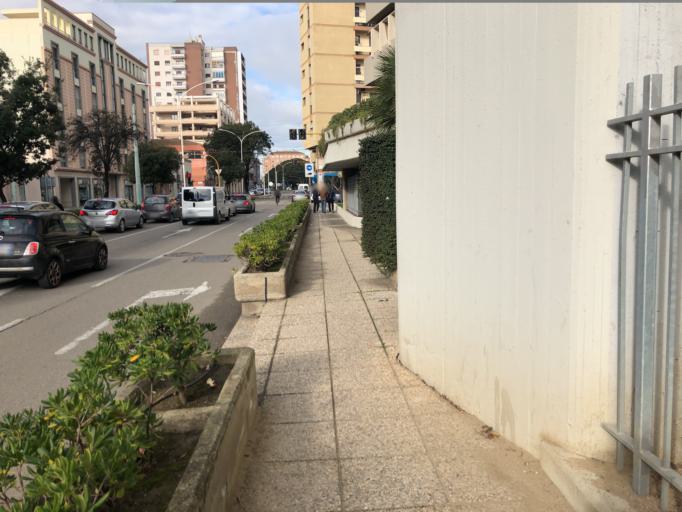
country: IT
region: Sardinia
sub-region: Provincia di Cagliari
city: Cagliari
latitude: 39.2104
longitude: 9.1196
